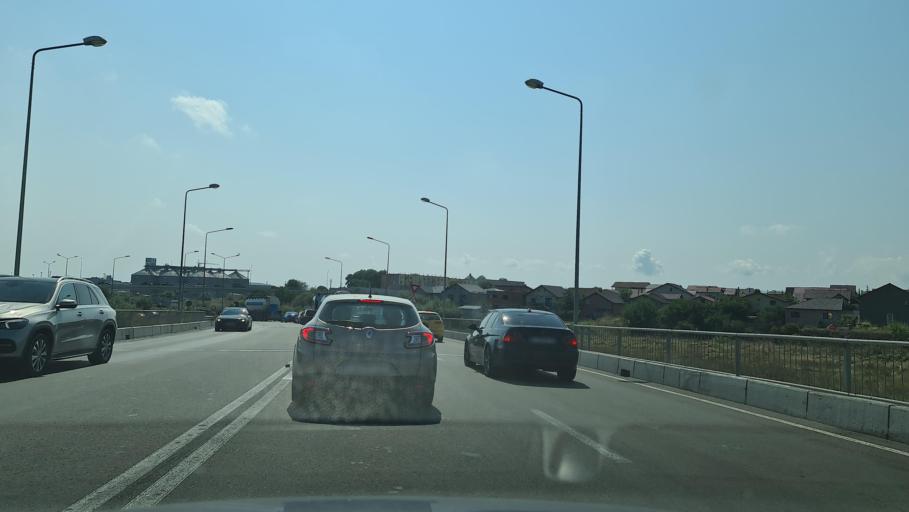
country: RO
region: Constanta
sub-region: Comuna Agigea
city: Agigea
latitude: 44.0967
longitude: 28.6361
